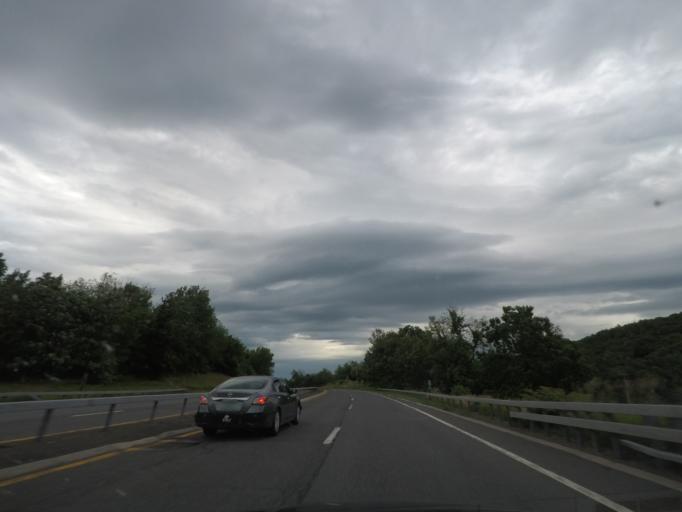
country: US
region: New York
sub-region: Dutchess County
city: Pine Plains
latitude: 42.0737
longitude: -73.7170
